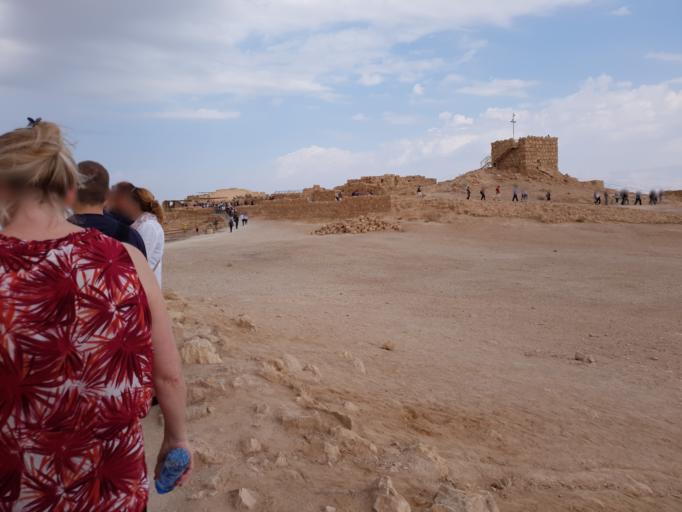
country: IL
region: Southern District
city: `En Boqeq
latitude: 31.3170
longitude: 35.3529
